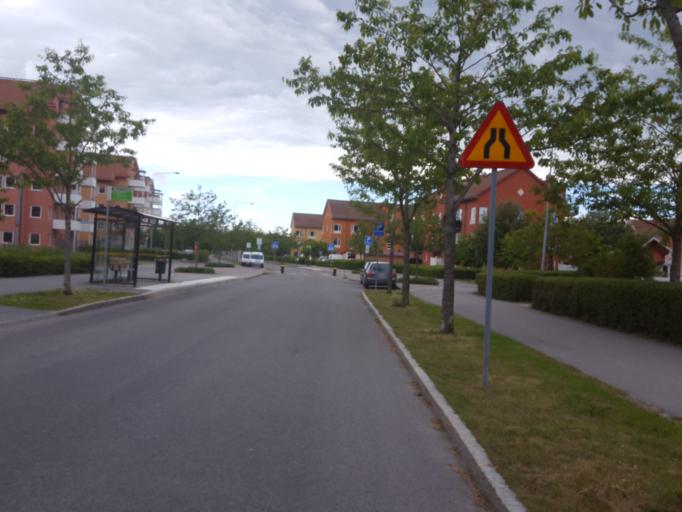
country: SE
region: Uppsala
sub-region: Uppsala Kommun
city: Saevja
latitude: 59.8613
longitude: 17.7093
